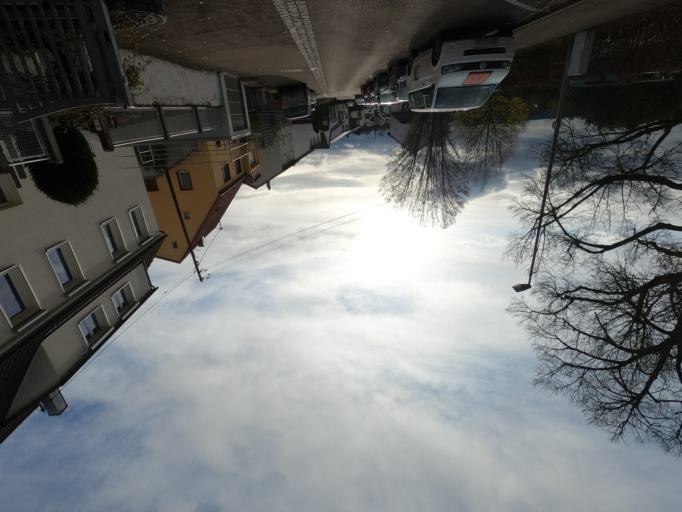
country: DE
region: Baden-Wuerttemberg
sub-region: Regierungsbezirk Stuttgart
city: Albershausen
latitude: 48.6956
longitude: 9.5670
